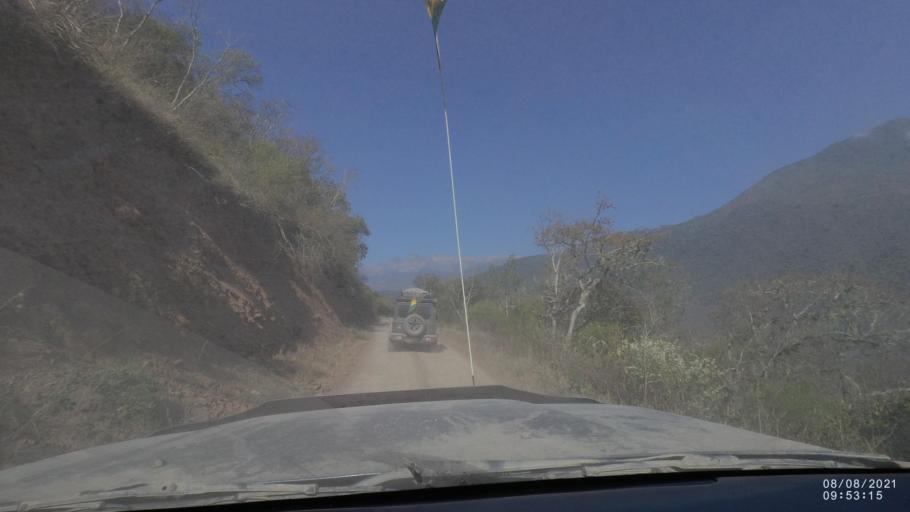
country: BO
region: La Paz
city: Quime
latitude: -16.6278
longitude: -66.7324
